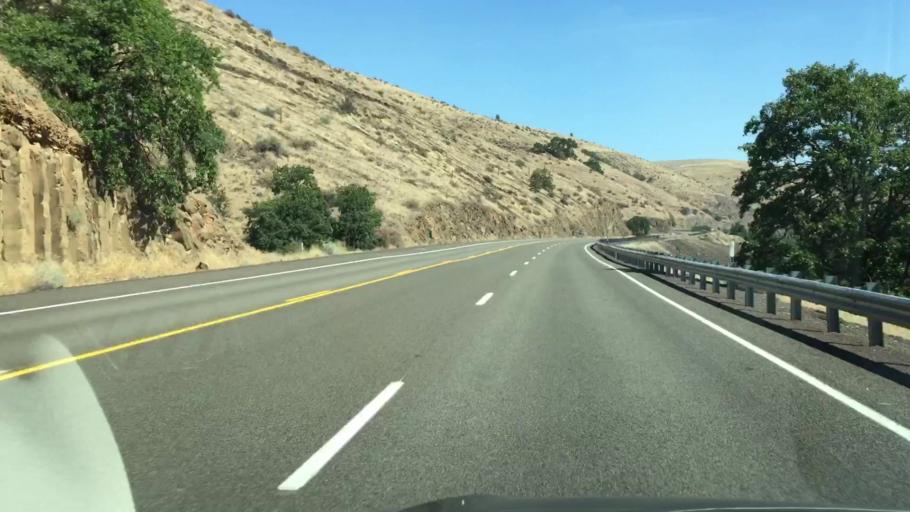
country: US
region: Oregon
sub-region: Wasco County
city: The Dalles
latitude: 45.2858
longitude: -121.1842
